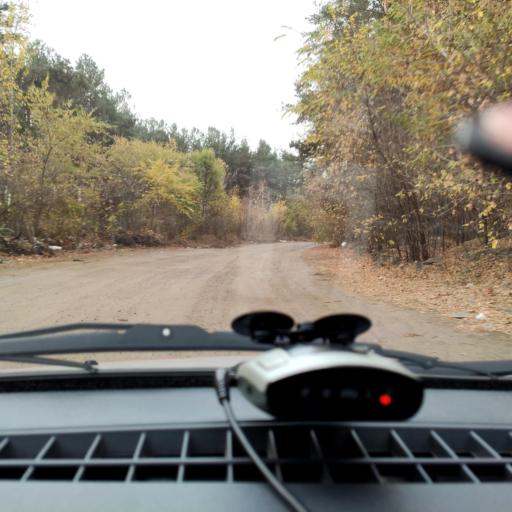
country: RU
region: Voronezj
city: Pridonskoy
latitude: 51.6749
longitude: 39.1253
